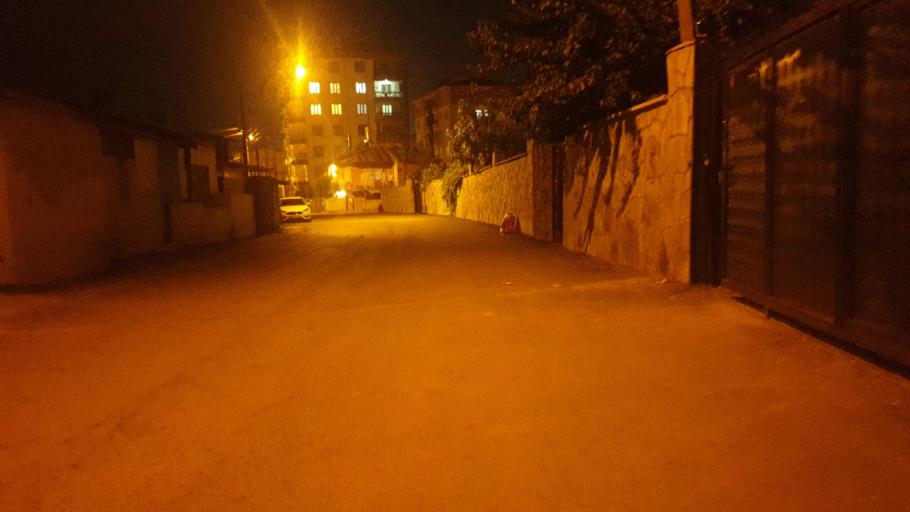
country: TR
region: Van
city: Van
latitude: 38.4884
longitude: 43.3883
